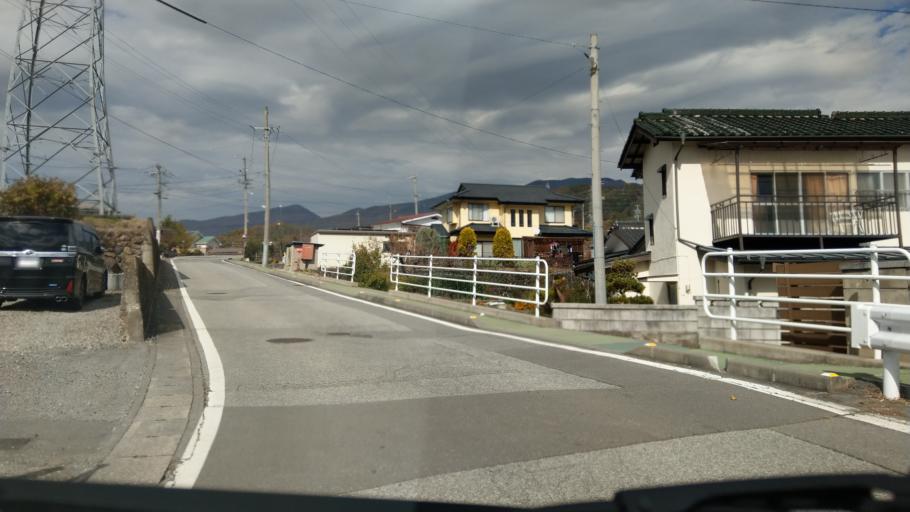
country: JP
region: Nagano
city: Komoro
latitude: 36.3343
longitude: 138.4162
